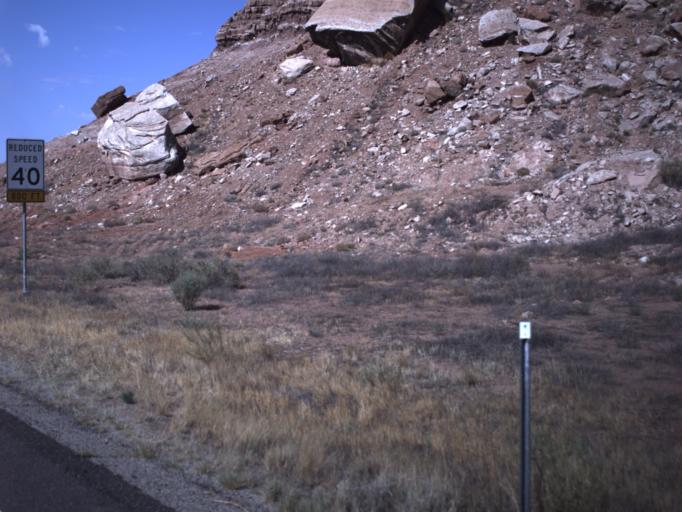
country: US
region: Utah
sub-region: San Juan County
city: Blanding
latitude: 37.2871
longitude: -109.5448
